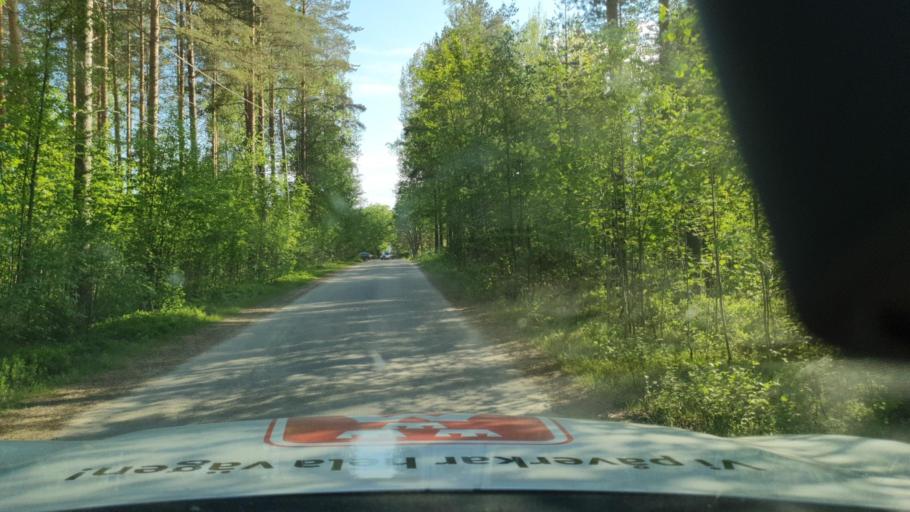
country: SE
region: Vaesterbotten
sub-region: Umea Kommun
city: Roback
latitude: 63.8429
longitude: 20.1202
